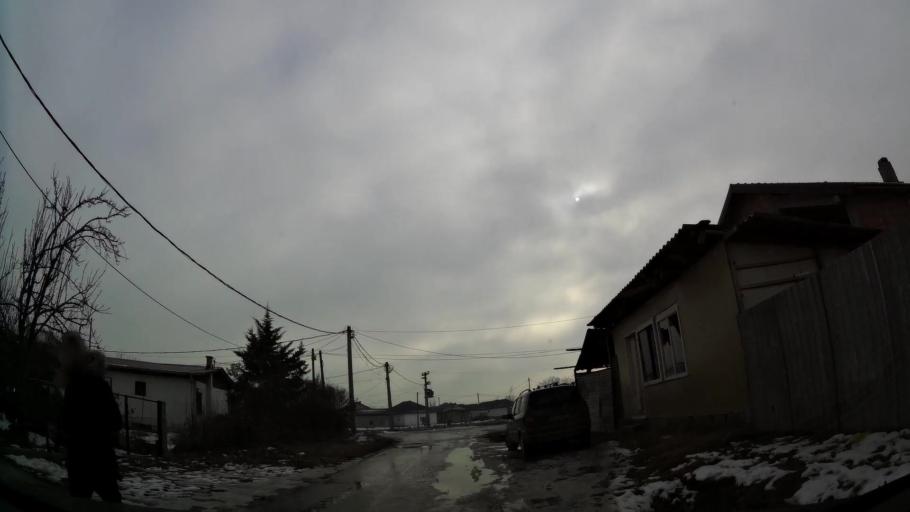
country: MK
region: Ilinden
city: Ilinden
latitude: 41.9919
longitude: 21.5715
